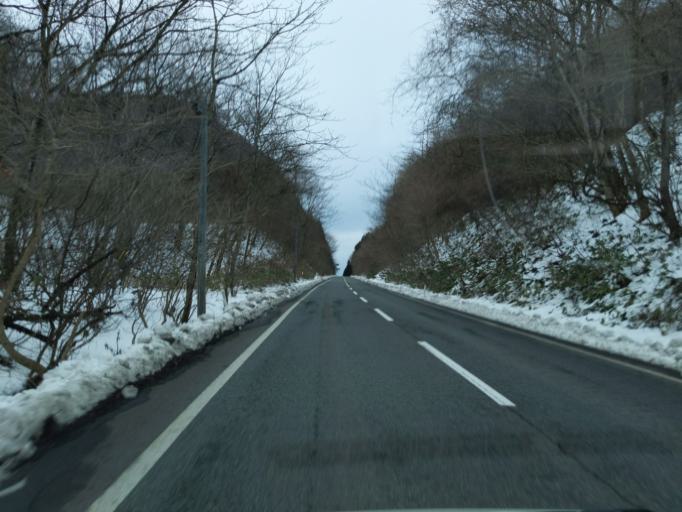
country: JP
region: Iwate
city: Mizusawa
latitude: 39.0930
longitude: 141.2705
